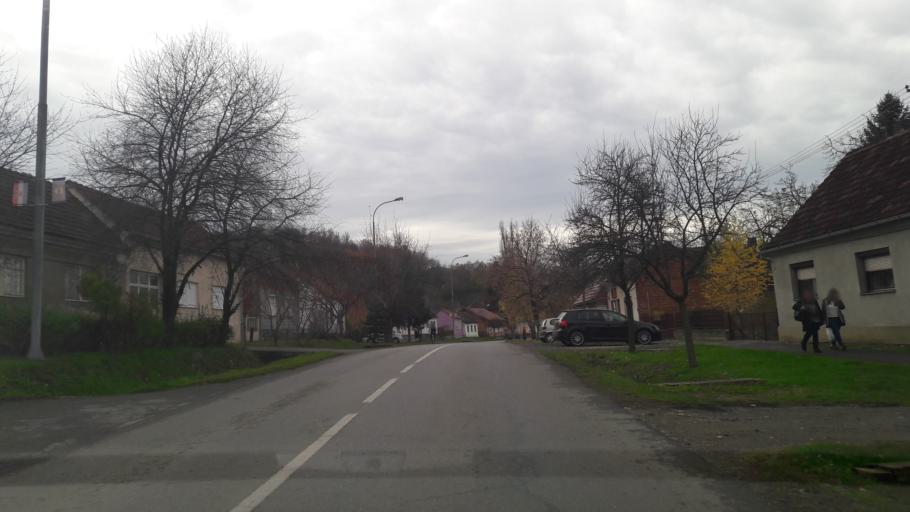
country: HR
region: Virovitick-Podravska
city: Orahovica
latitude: 45.5373
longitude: 17.8926
